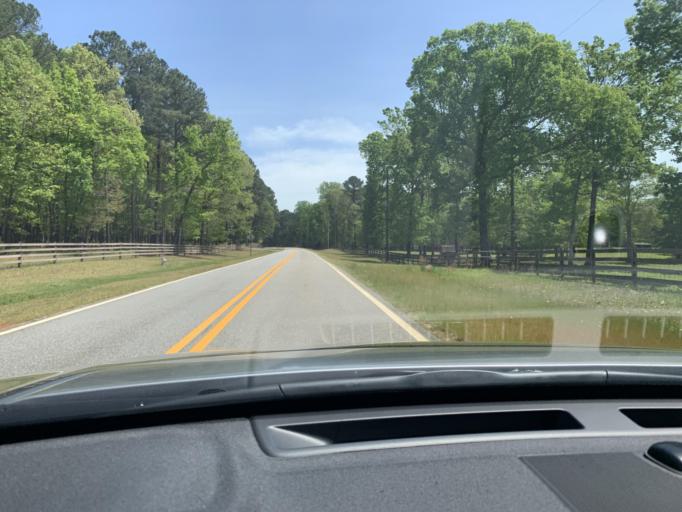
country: US
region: Georgia
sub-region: Oconee County
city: Bogart
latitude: 33.8731
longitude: -83.5646
